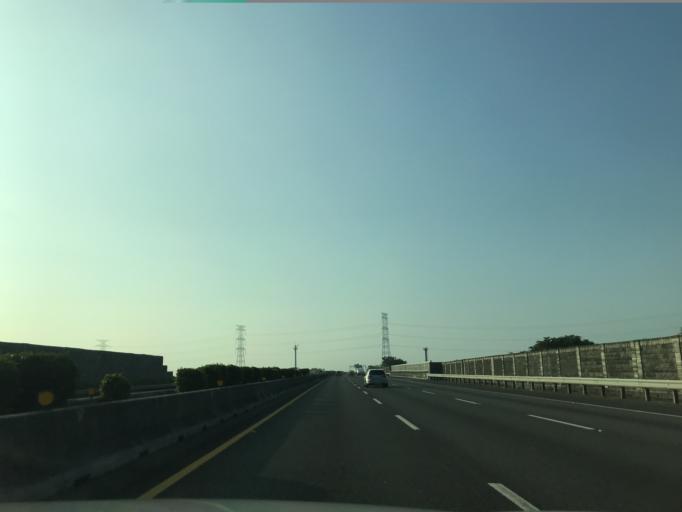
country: TW
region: Taiwan
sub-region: Yunlin
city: Douliu
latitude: 23.8236
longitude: 120.4852
